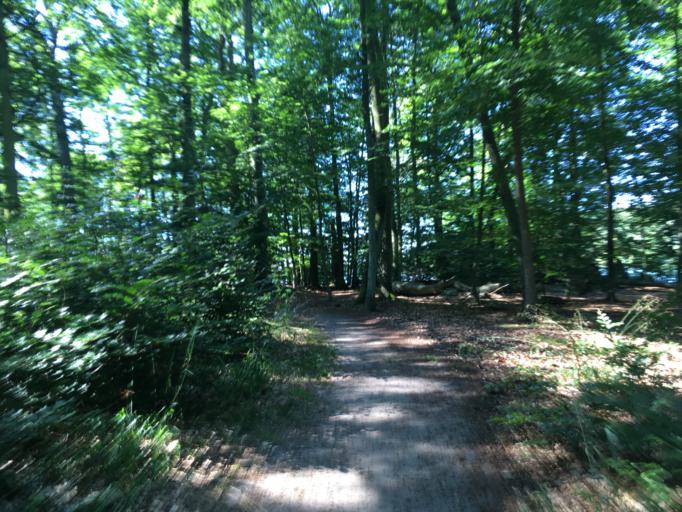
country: DE
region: Brandenburg
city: Furstenberg
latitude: 53.1682
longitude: 13.0387
